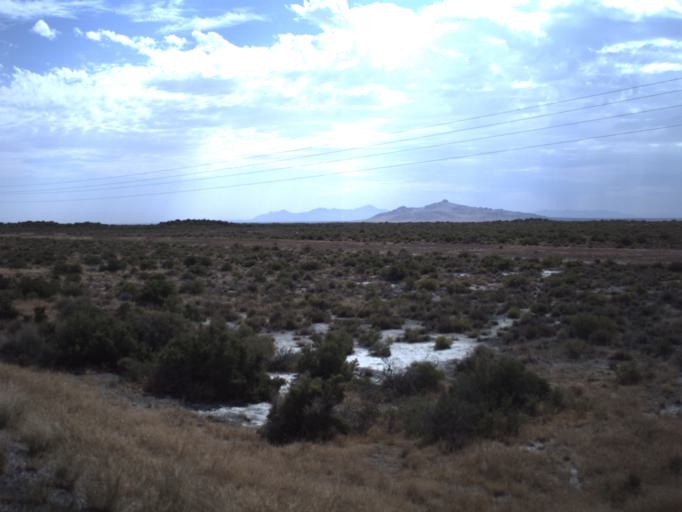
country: US
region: Utah
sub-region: Tooele County
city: Wendover
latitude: 41.4221
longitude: -113.8833
